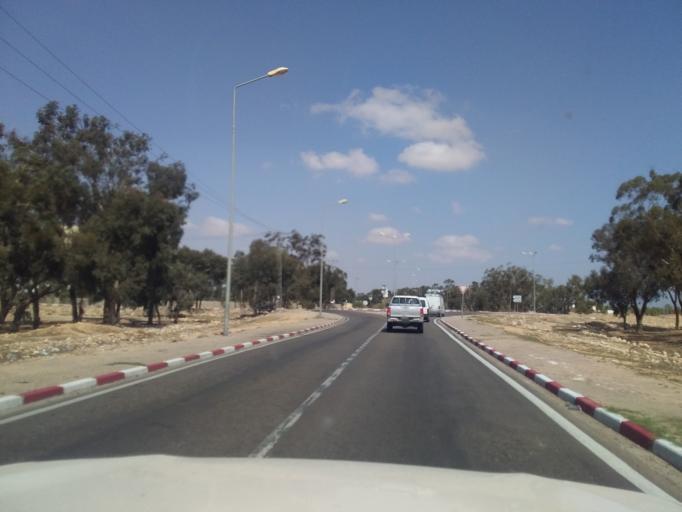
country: TN
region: Madanin
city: Medenine
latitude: 33.5982
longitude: 10.3098
